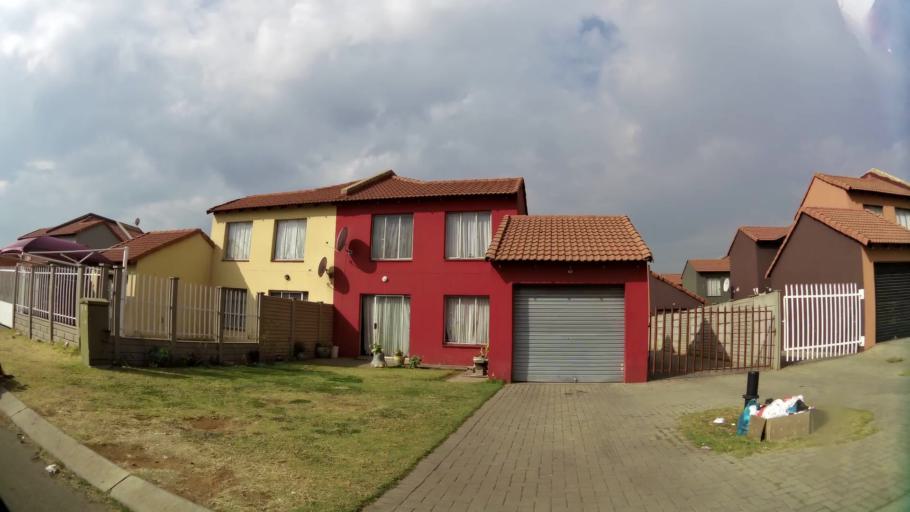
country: ZA
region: Gauteng
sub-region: Sedibeng District Municipality
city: Vanderbijlpark
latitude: -26.6791
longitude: 27.8394
